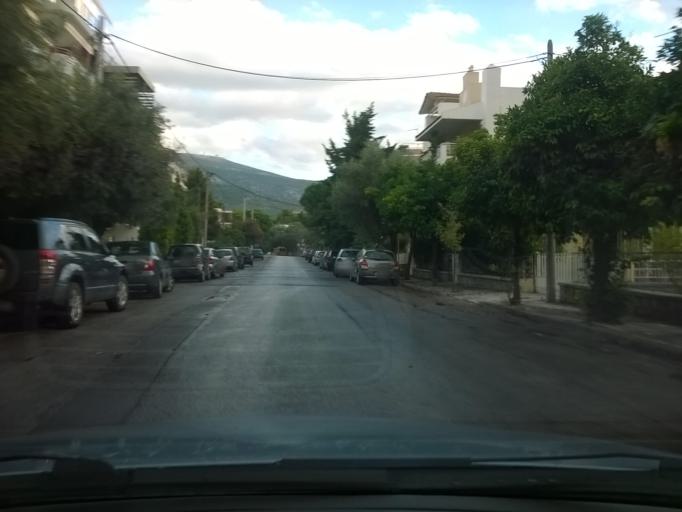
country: GR
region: Attica
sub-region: Nomarchia Athinas
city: Papagou
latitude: 37.9885
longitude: 23.7938
